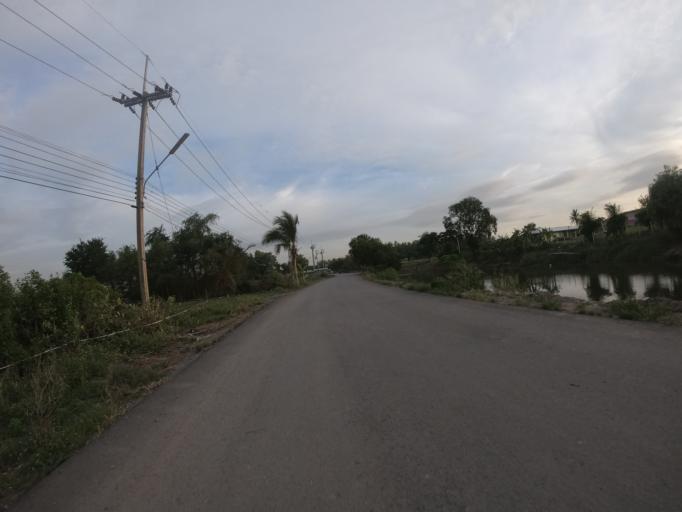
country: TH
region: Pathum Thani
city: Ban Lam Luk Ka
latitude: 14.0080
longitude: 100.7988
